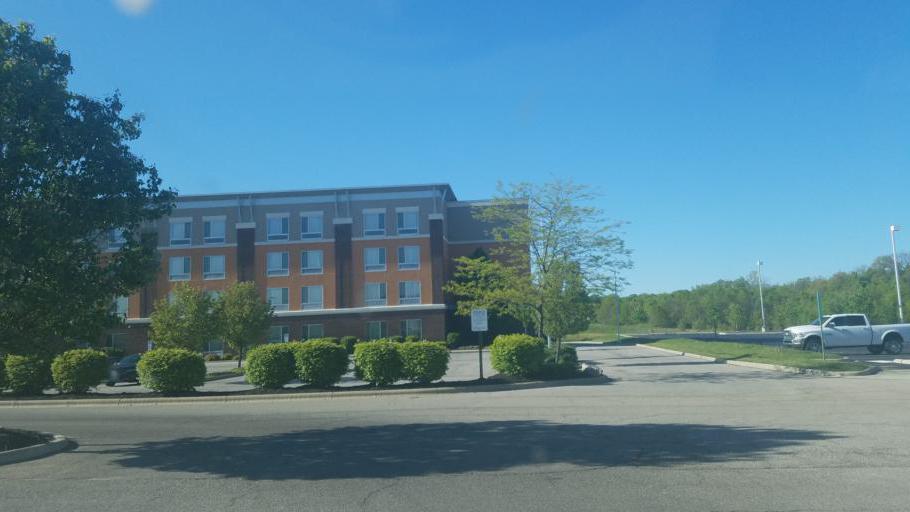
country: US
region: Ohio
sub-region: Franklin County
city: Westerville
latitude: 40.1500
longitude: -82.9735
